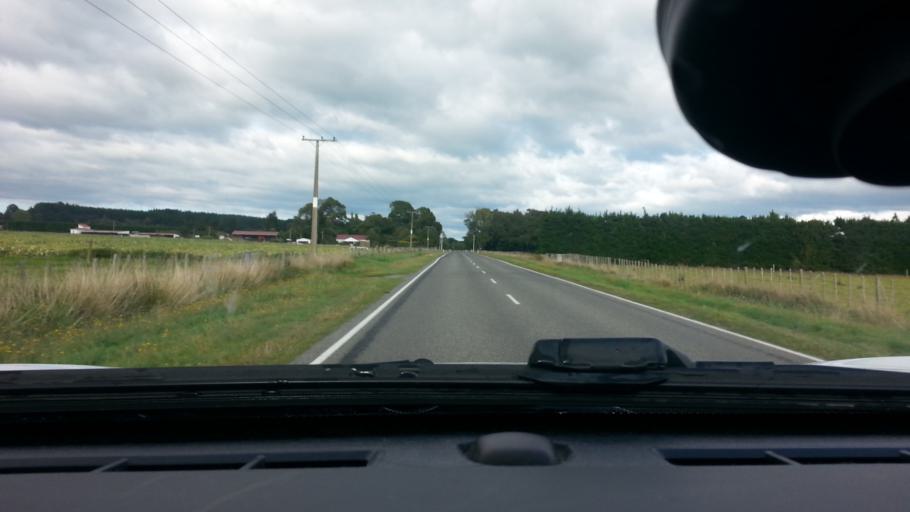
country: NZ
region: Wellington
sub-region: South Wairarapa District
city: Waipawa
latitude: -41.3146
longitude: 175.2613
